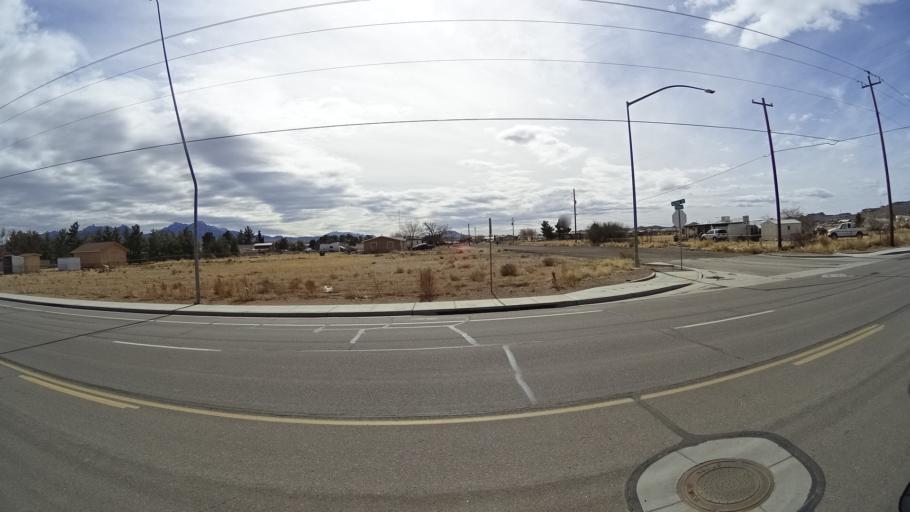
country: US
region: Arizona
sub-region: Mohave County
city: New Kingman-Butler
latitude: 35.2395
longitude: -114.0199
